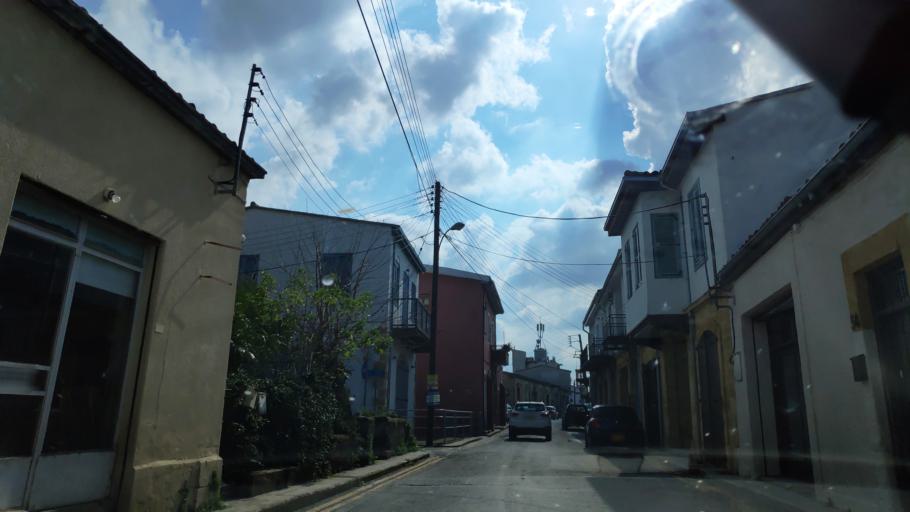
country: CY
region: Lefkosia
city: Nicosia
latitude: 35.1483
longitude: 33.3417
